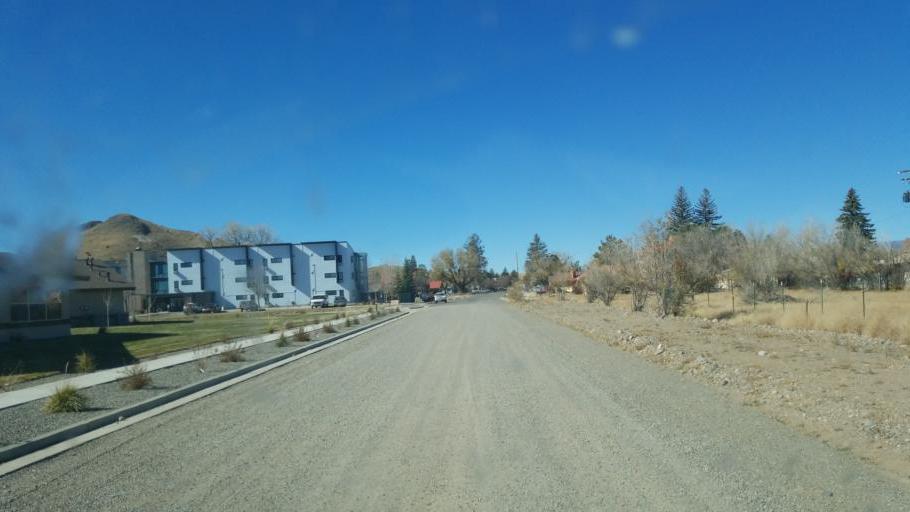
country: US
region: Colorado
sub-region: Rio Grande County
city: Del Norte
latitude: 37.6771
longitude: -106.3443
